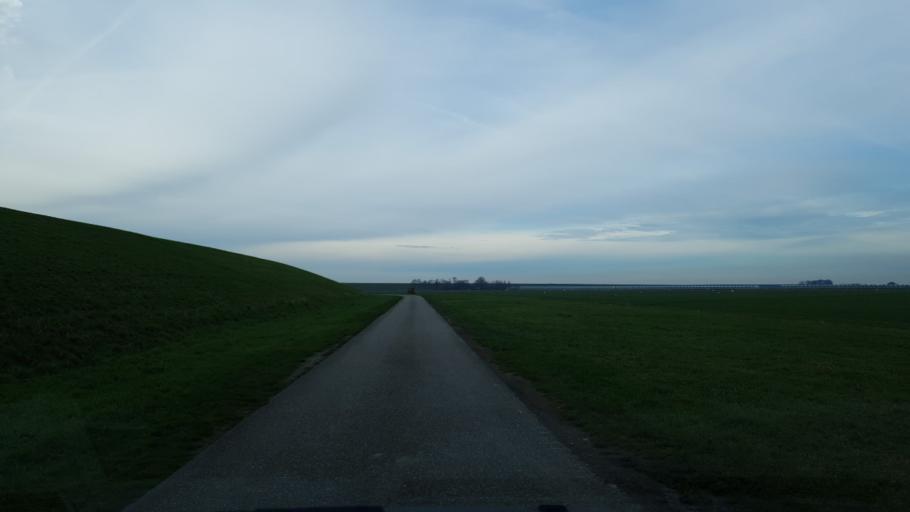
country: NL
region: North Brabant
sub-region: Gemeente Woensdrecht
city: Woensdrecht
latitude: 51.3990
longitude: 4.1619
